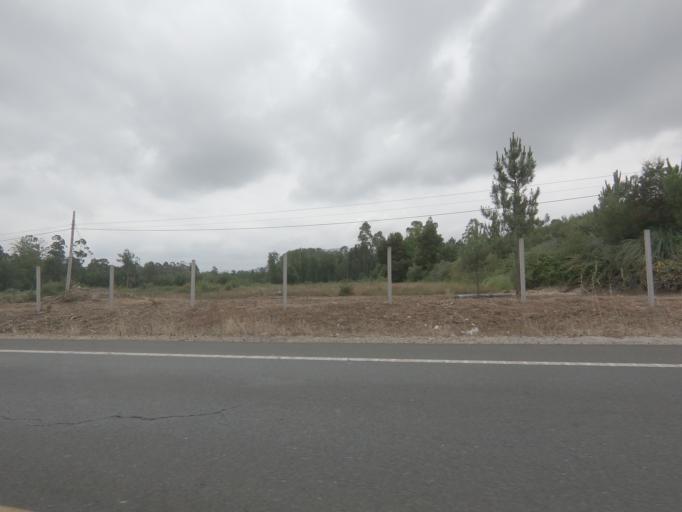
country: PT
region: Viana do Castelo
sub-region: Vila Nova de Cerveira
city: Vila Nova de Cerveira
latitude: 41.9556
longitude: -8.7654
